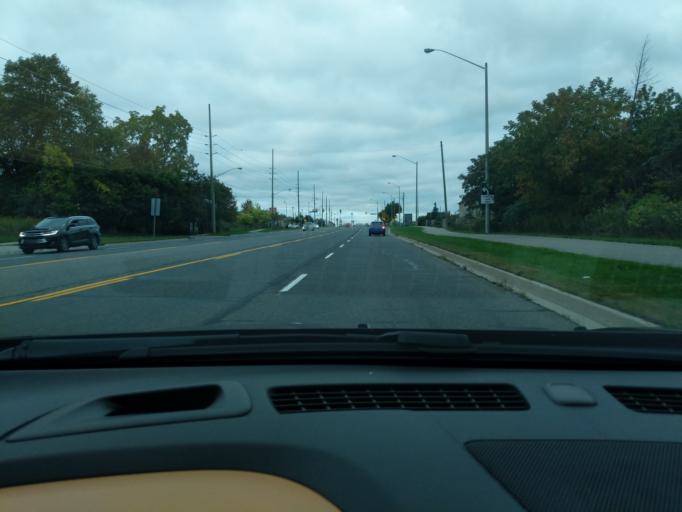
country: CA
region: Ontario
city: Vaughan
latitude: 43.8566
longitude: -79.4862
